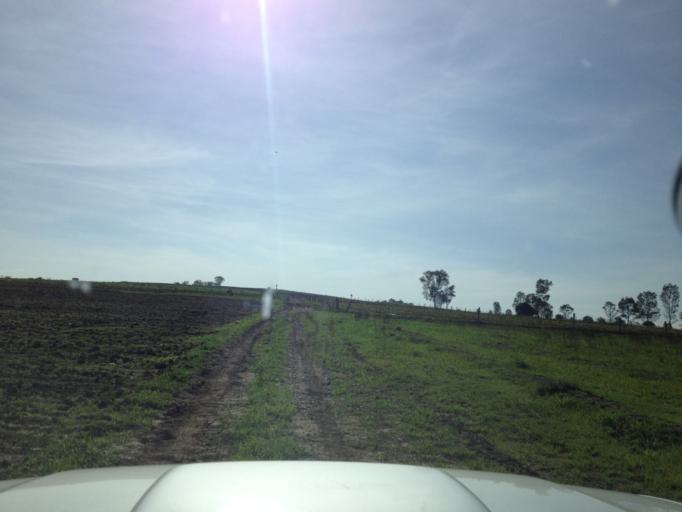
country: MX
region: Michoacan
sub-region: Tarimbaro
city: Pena del Panal
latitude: 19.7678
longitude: -101.1902
